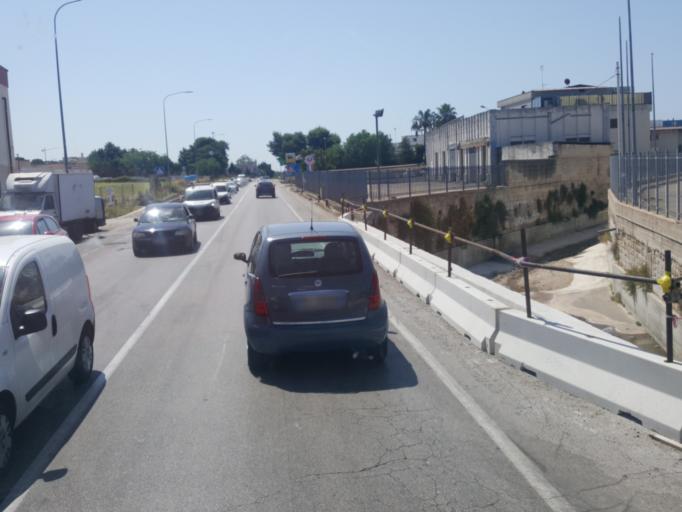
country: IT
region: Apulia
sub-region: Provincia di Taranto
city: Massafra
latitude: 40.5846
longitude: 17.1096
